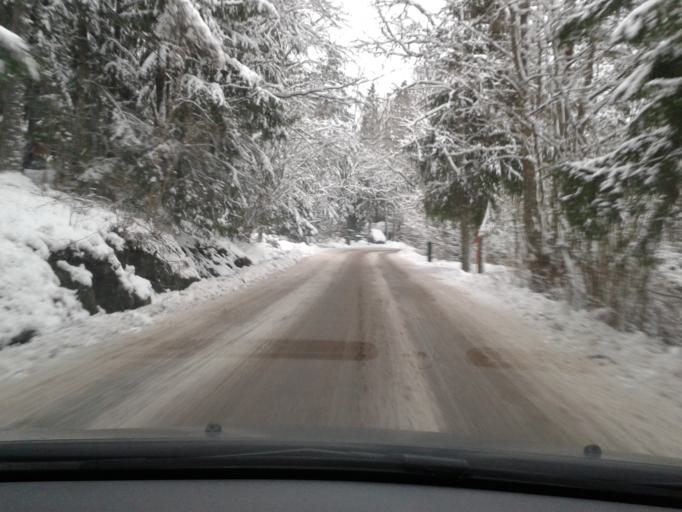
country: SE
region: Stockholm
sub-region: Nacka Kommun
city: Saltsjobaden
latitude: 59.2277
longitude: 18.3032
